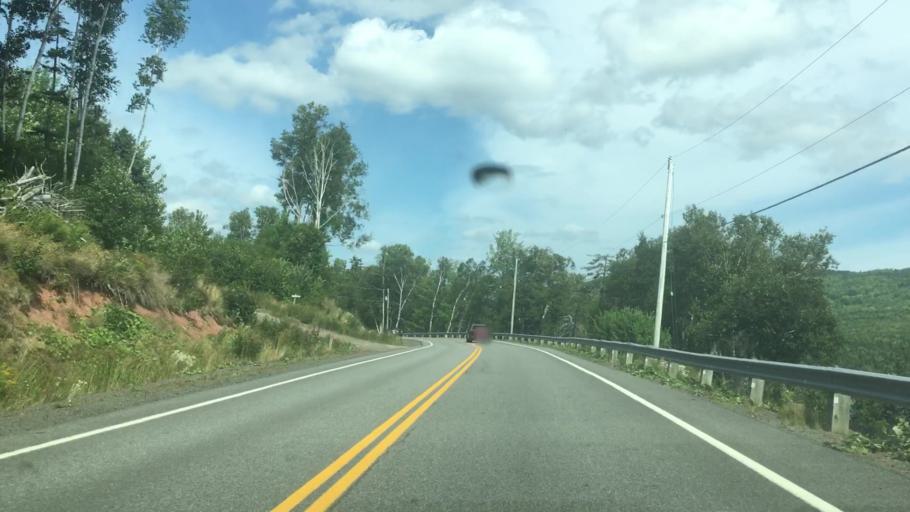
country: CA
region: Nova Scotia
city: Sydney Mines
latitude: 46.2672
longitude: -60.6086
